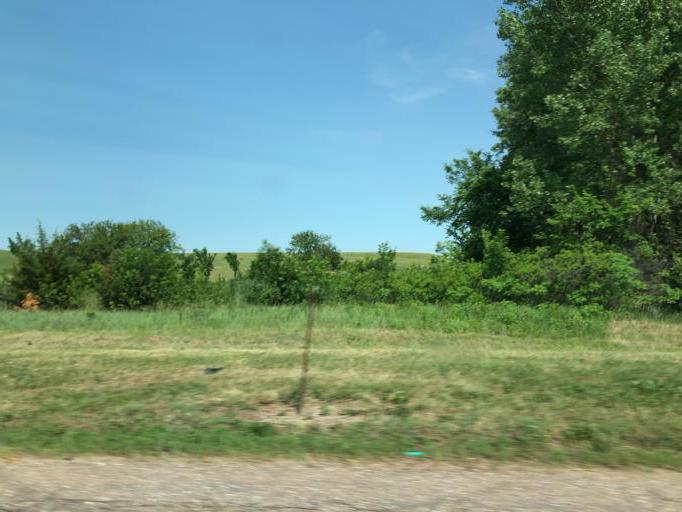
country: US
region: Nebraska
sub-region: Thayer County
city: Hebron
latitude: 40.1626
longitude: -97.5706
